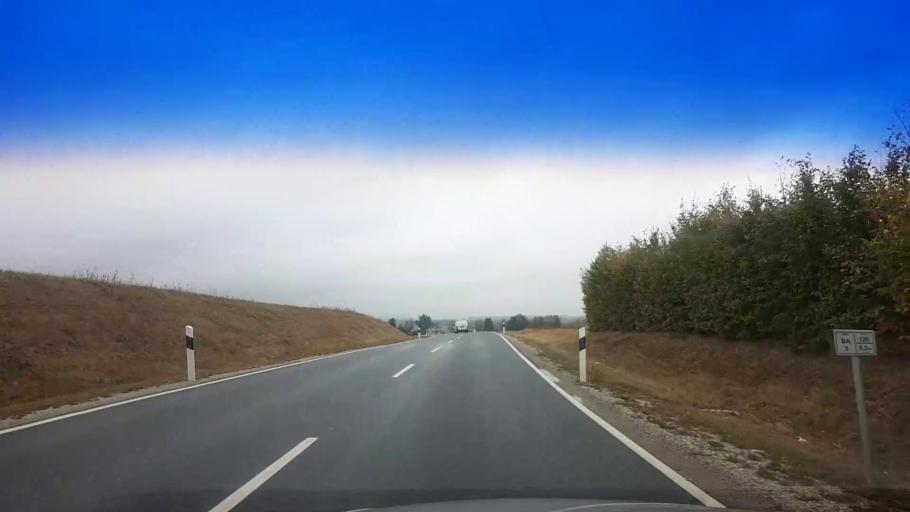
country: DE
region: Bavaria
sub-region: Upper Franconia
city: Buttenheim
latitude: 49.7960
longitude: 11.0351
